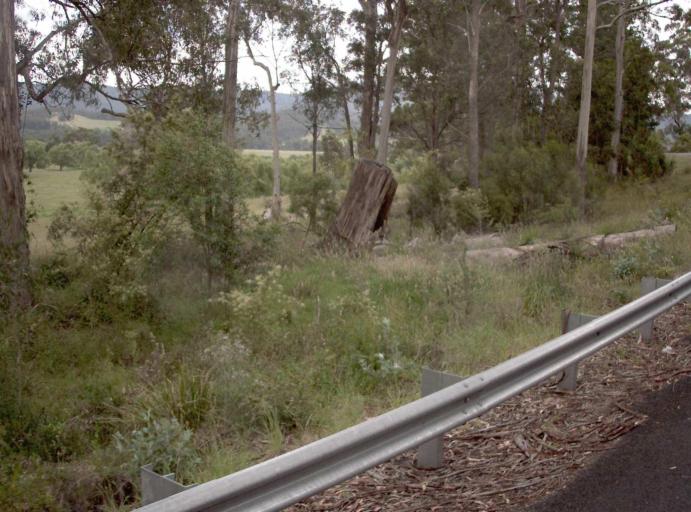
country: AU
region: New South Wales
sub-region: Bombala
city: Bombala
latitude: -37.5049
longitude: 149.1777
